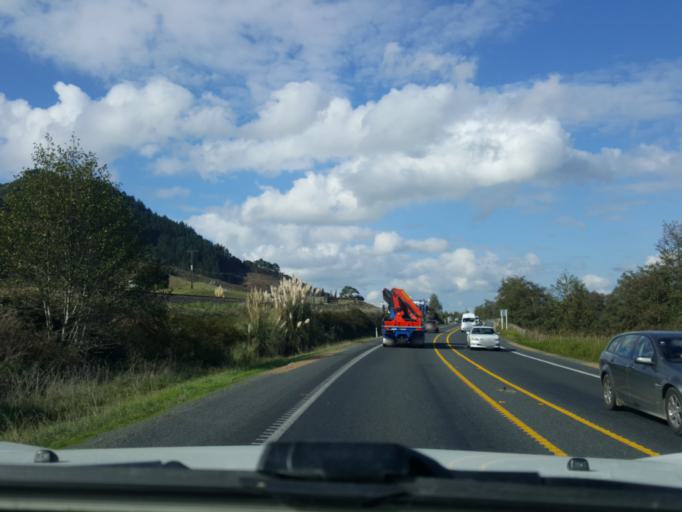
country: NZ
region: Waikato
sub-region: Waikato District
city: Ngaruawahia
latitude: -37.6019
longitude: 175.1715
